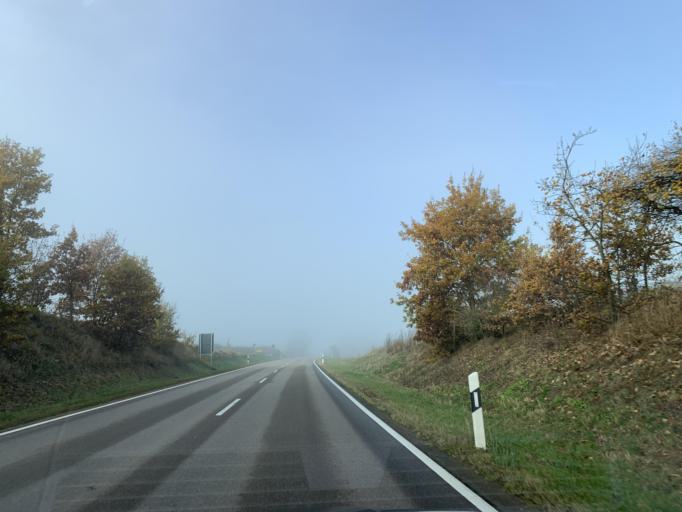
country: DE
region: Bavaria
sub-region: Upper Palatinate
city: Brunn
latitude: 49.2394
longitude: 12.1936
